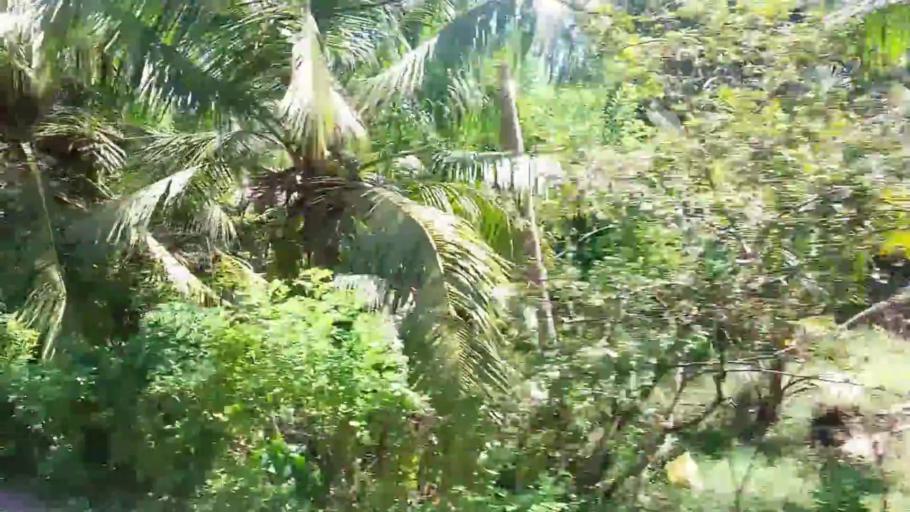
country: LK
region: Southern
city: Hikkaduwa
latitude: 6.1753
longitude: 80.0824
